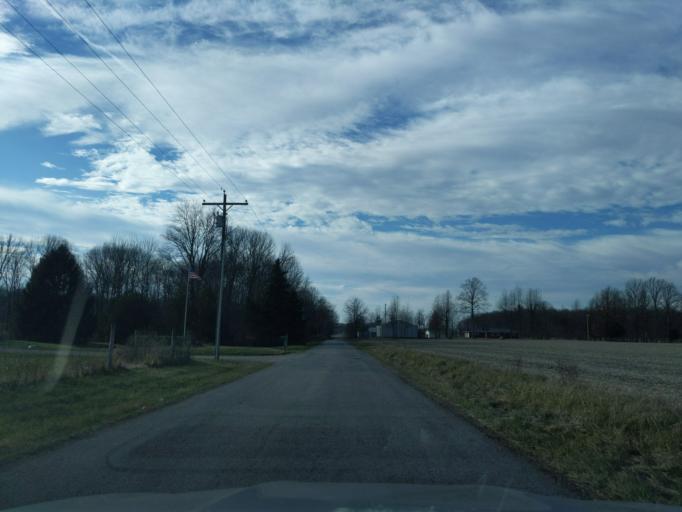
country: US
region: Indiana
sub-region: Decatur County
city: Greensburg
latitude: 39.2636
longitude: -85.4210
